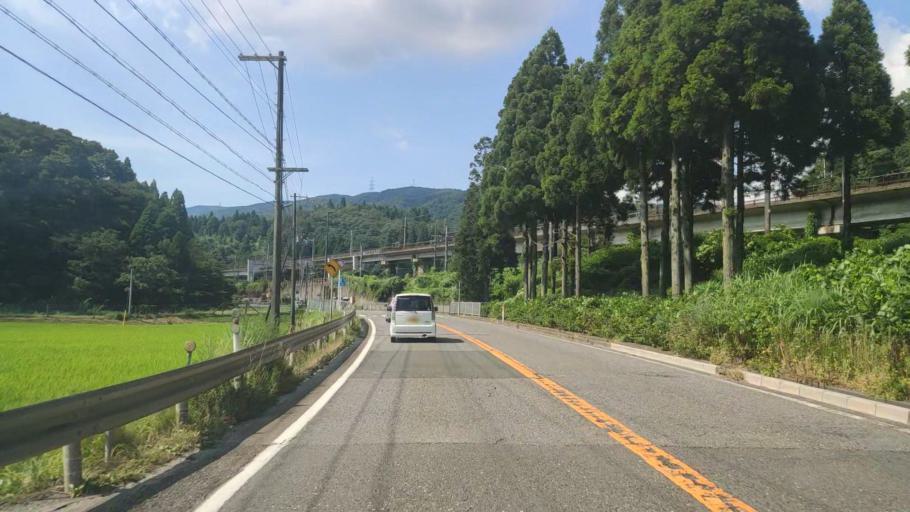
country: JP
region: Fukui
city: Tsuruga
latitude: 35.5486
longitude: 136.1477
